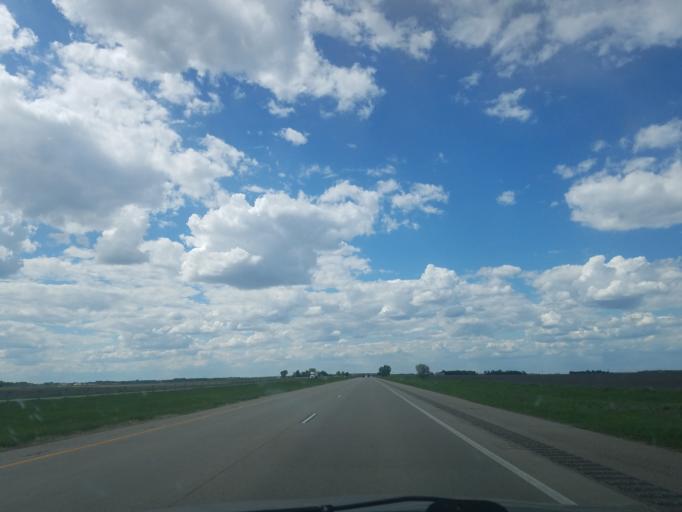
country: US
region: Minnesota
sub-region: Clay County
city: Glyndon
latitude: 46.7965
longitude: -96.5742
